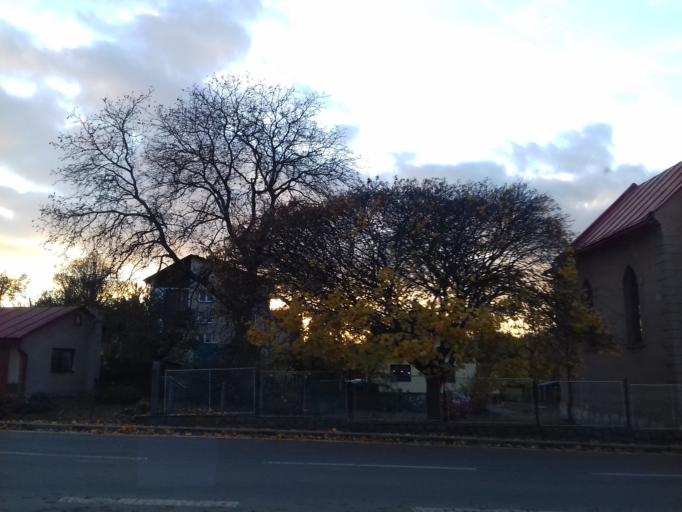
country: CZ
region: Pardubicky
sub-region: Okres Chrudim
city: Hlinsko
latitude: 49.7925
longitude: 15.9245
